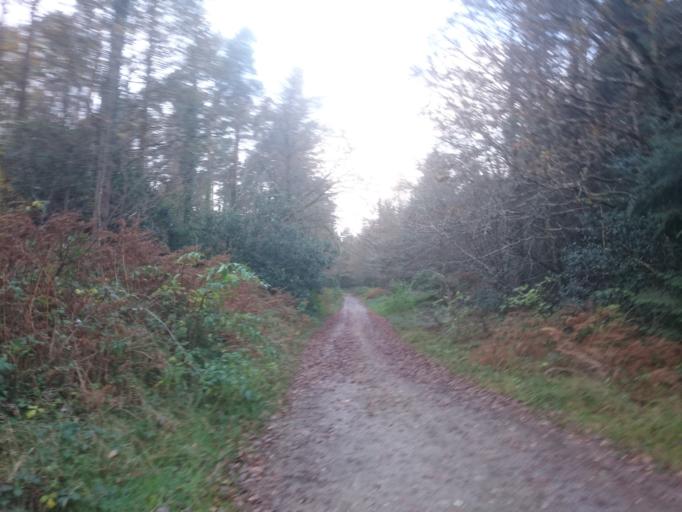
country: IE
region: Leinster
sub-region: Kilkenny
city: Thomastown
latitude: 52.4698
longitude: -7.0592
